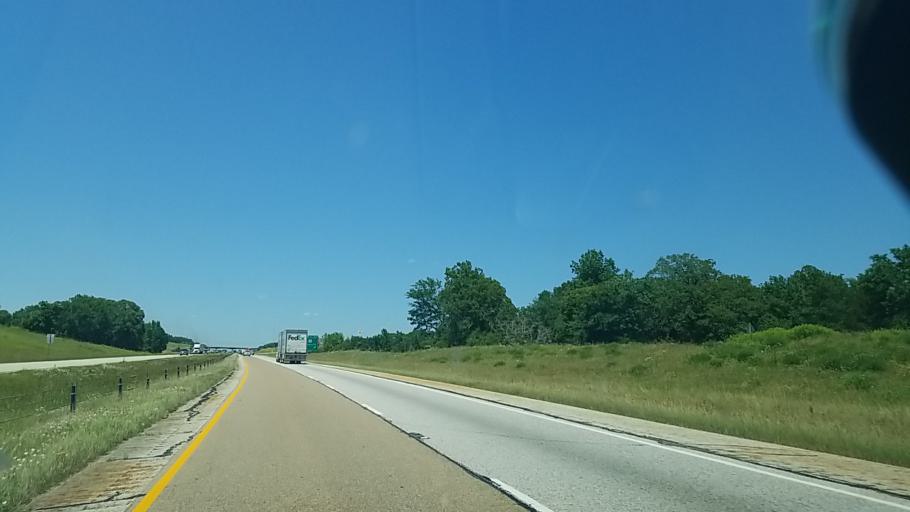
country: US
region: Texas
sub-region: Leon County
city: Centerville
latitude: 31.2495
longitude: -95.9888
